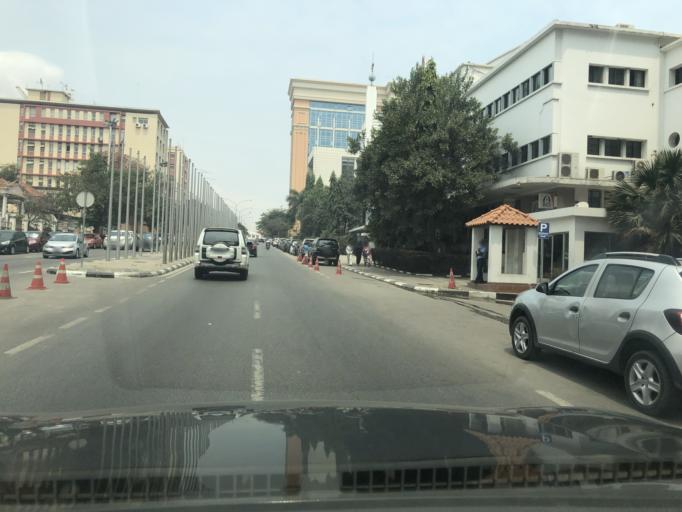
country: AO
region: Luanda
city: Luanda
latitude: -8.8190
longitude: 13.2287
